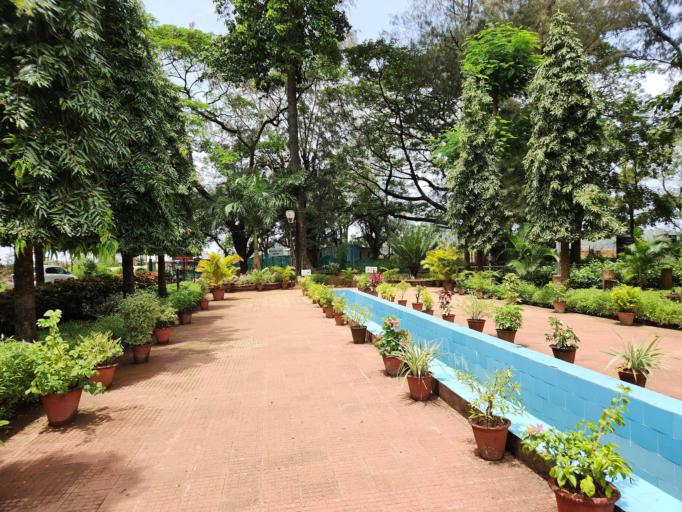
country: IN
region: Goa
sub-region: North Goa
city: Panaji
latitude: 15.4960
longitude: 73.8184
